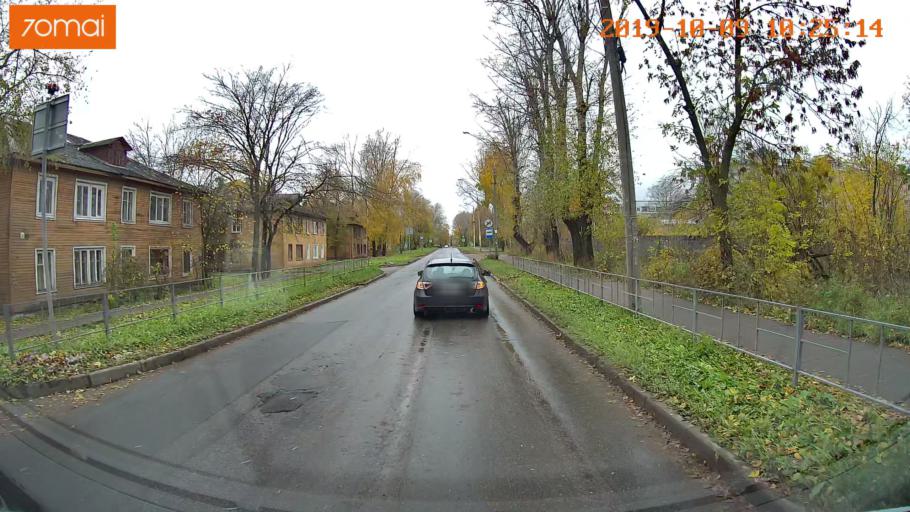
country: RU
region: Vologda
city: Vologda
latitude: 59.2128
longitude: 39.9339
